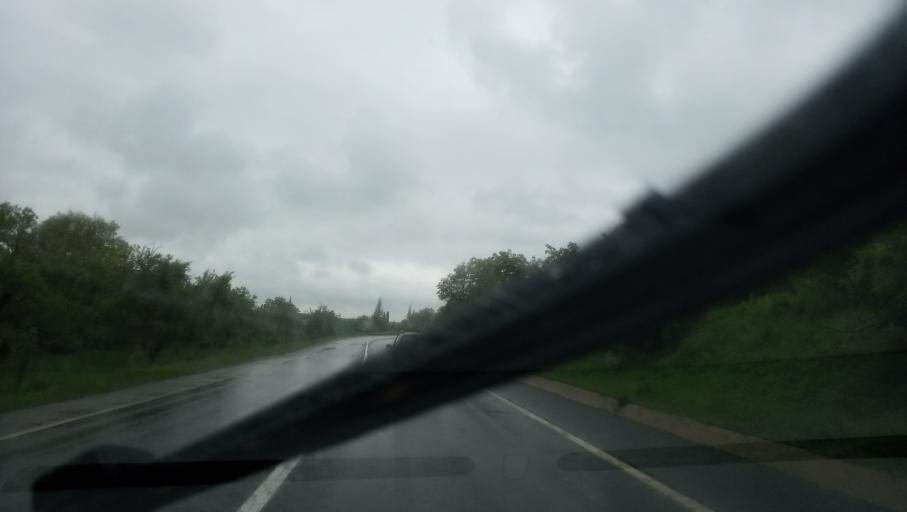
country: RO
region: Sibiu
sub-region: Comuna Apoldu de Jos
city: Apoldu de Jos
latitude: 45.8421
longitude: 23.8373
